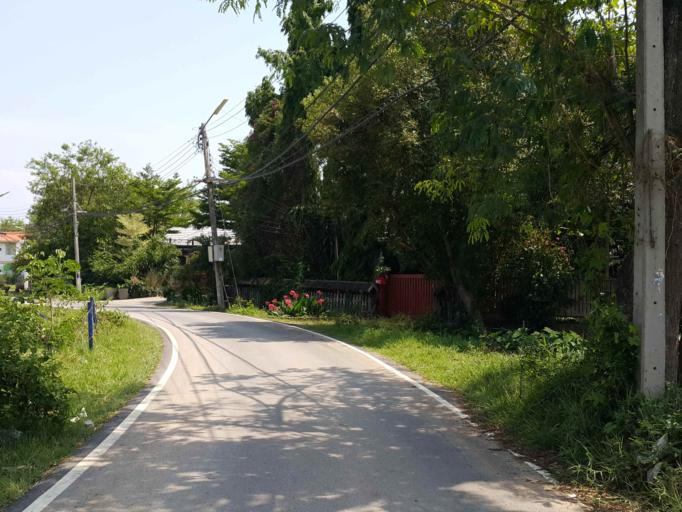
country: TH
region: Chiang Mai
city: Chiang Mai
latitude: 18.7538
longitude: 98.9552
